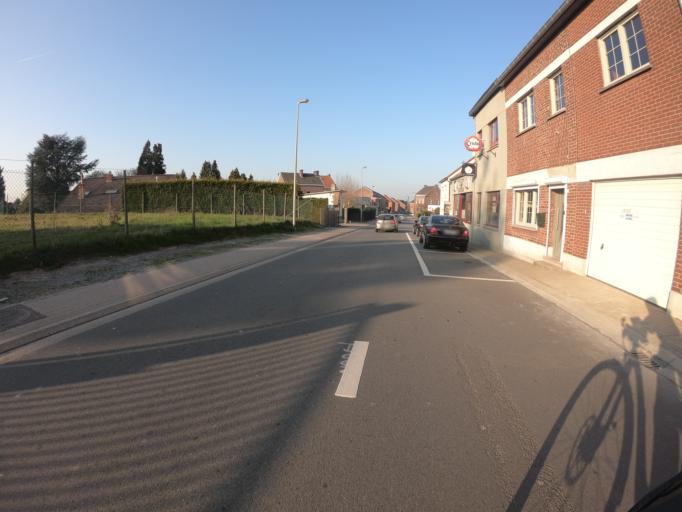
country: BE
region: Flanders
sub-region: Provincie Limburg
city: Heers
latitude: 50.8072
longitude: 5.2871
